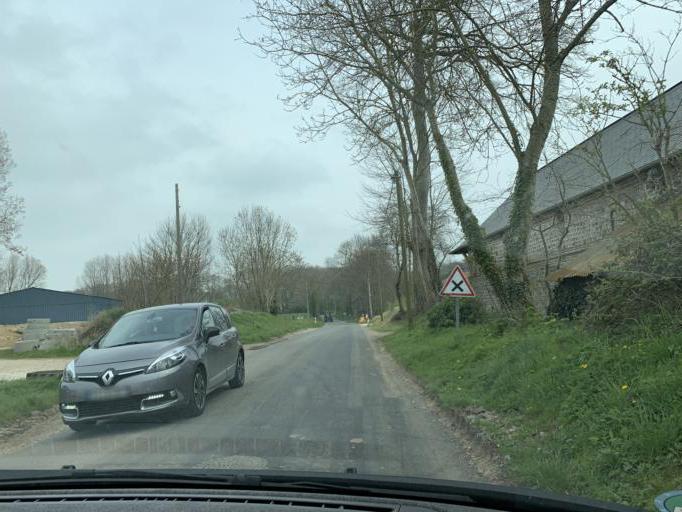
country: FR
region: Haute-Normandie
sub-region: Departement de la Seine-Maritime
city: Saint-Valery-en-Caux
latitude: 49.8579
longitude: 0.7541
